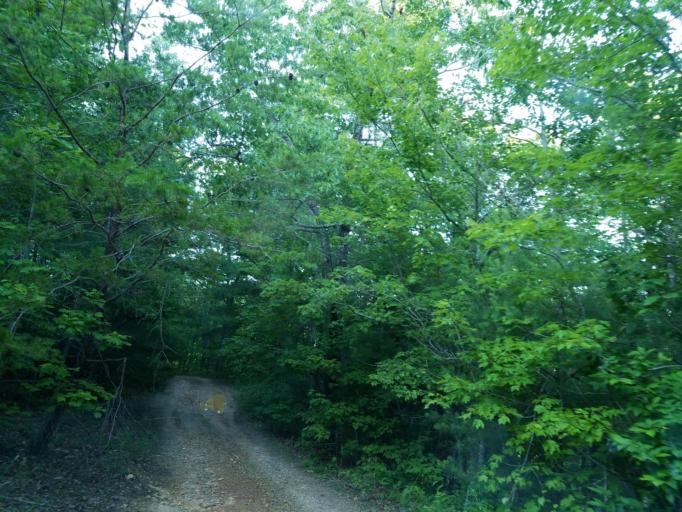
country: US
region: Georgia
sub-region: Fannin County
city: Blue Ridge
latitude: 34.8116
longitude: -84.1584
